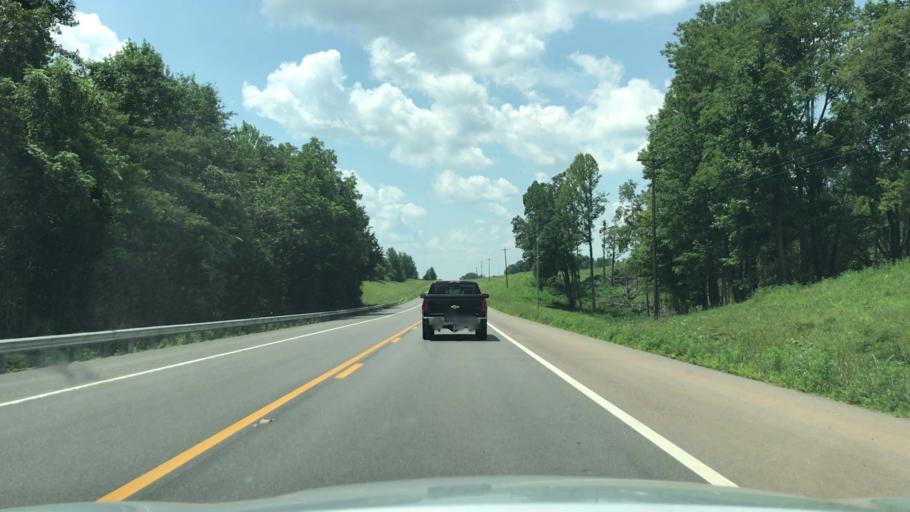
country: US
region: Tennessee
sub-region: Pickett County
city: Byrdstown
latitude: 36.5079
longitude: -85.1738
